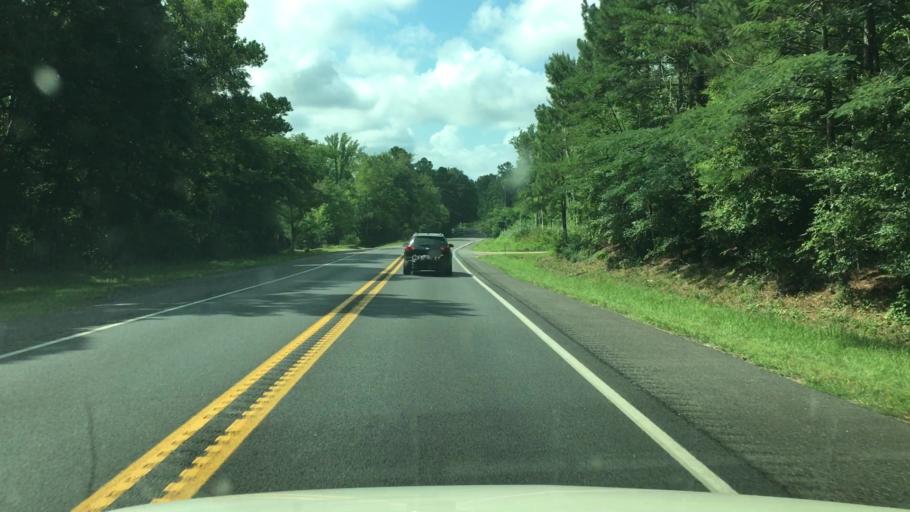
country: US
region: Arkansas
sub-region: Garland County
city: Lake Hamilton
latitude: 34.3506
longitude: -93.1842
